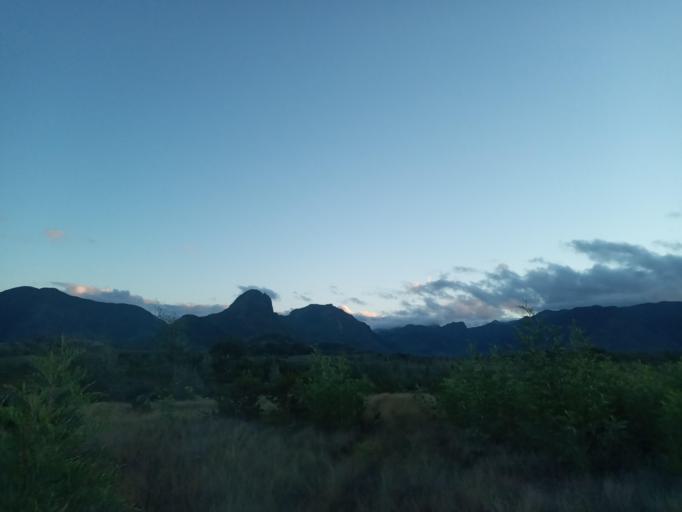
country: MG
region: Anosy
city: Fort Dauphin
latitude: -24.5111
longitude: 47.2245
